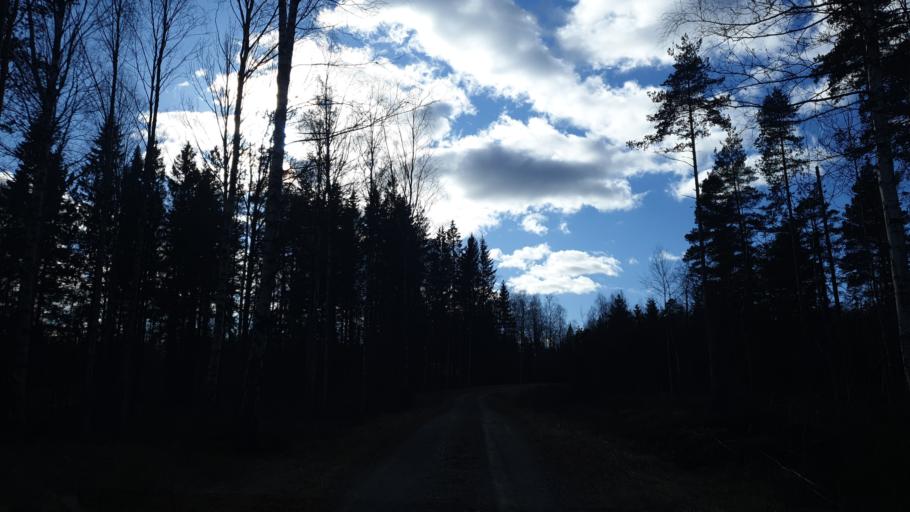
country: SE
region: OErebro
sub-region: Orebro Kommun
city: Garphyttan
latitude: 59.3701
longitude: 14.9707
